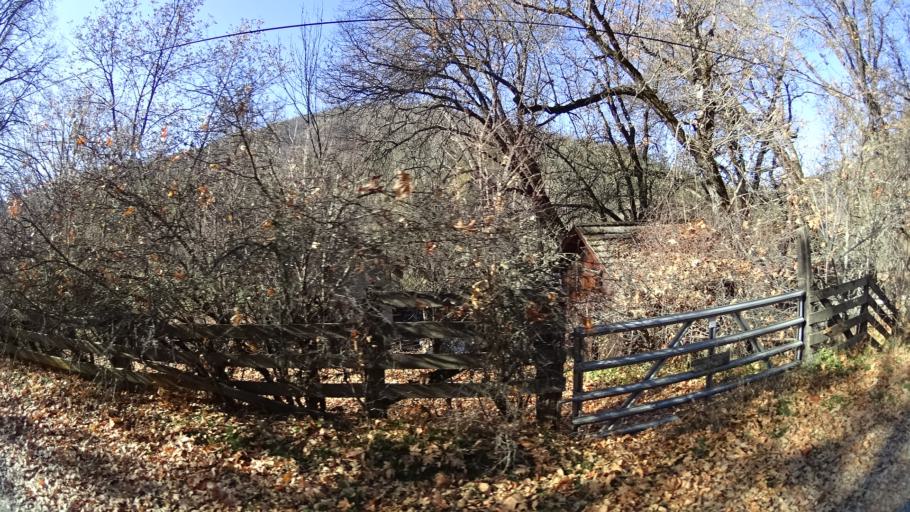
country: US
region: California
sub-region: Siskiyou County
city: Happy Camp
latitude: 41.8358
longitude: -123.0067
